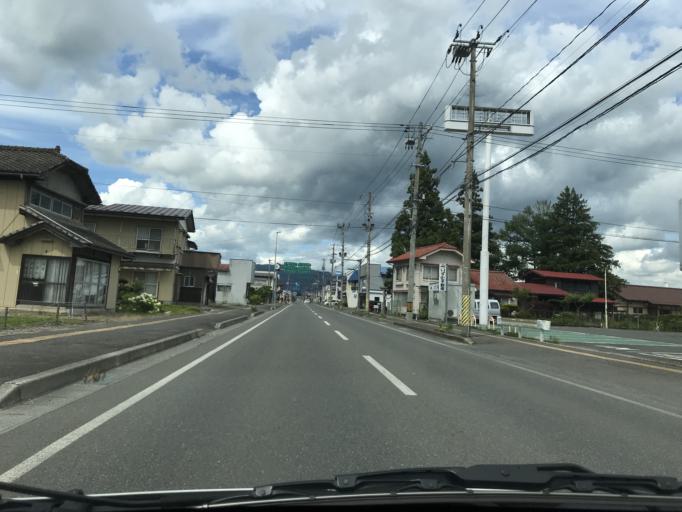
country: JP
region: Iwate
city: Tono
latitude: 39.3364
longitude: 141.5377
